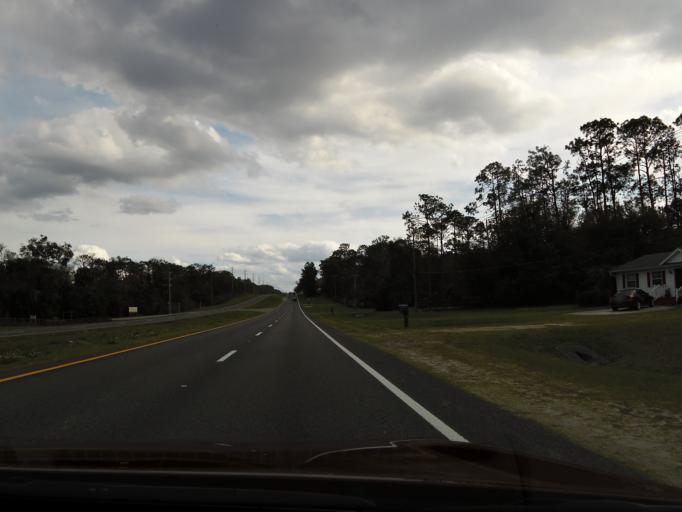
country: US
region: Florida
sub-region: Volusia County
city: De Leon Springs
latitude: 29.1022
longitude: -81.3394
